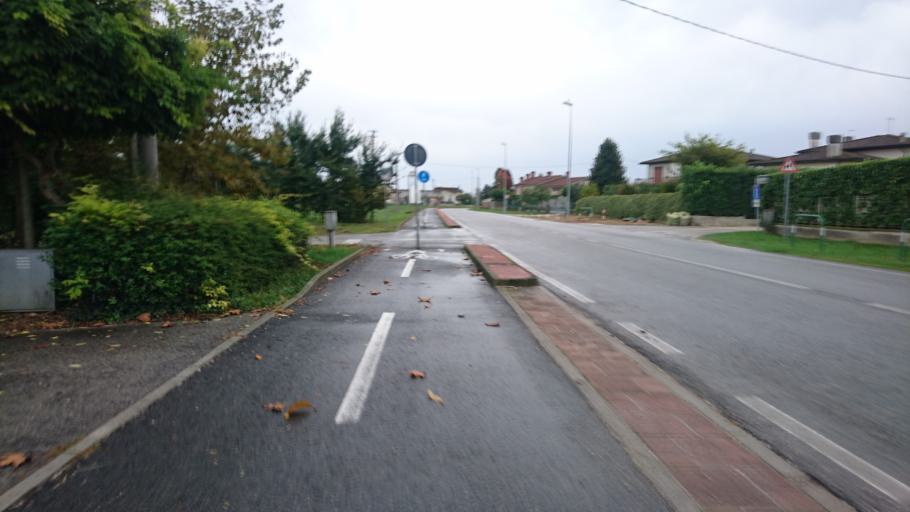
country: IT
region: Veneto
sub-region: Provincia di Padova
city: Veggiano
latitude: 45.4533
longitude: 11.7046
